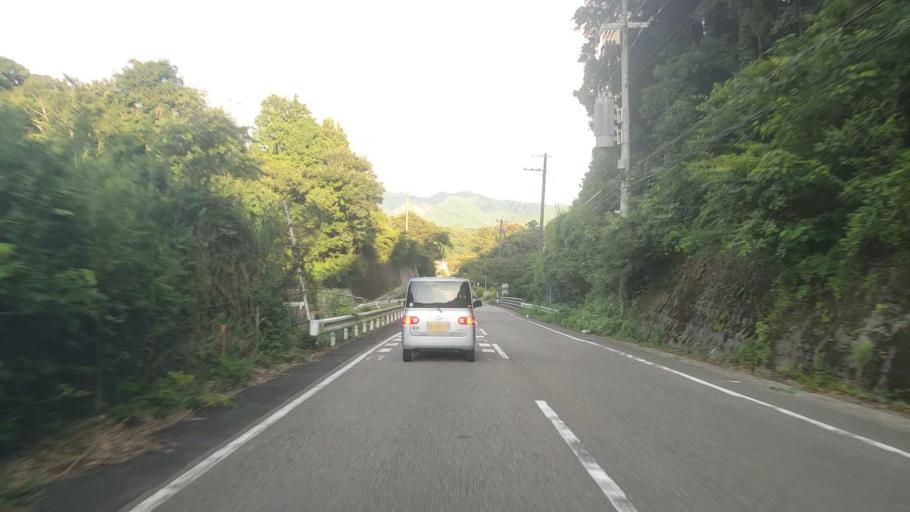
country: JP
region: Wakayama
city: Tanabe
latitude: 33.7274
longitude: 135.4383
